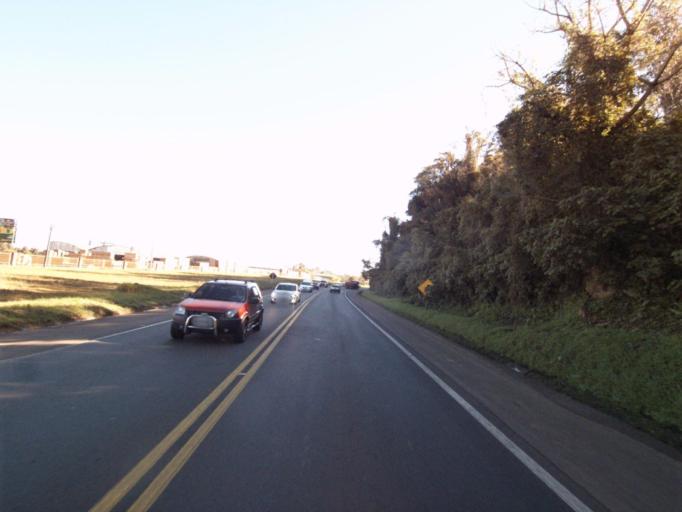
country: BR
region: Santa Catarina
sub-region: Chapeco
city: Chapeco
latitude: -26.9640
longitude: -52.5606
